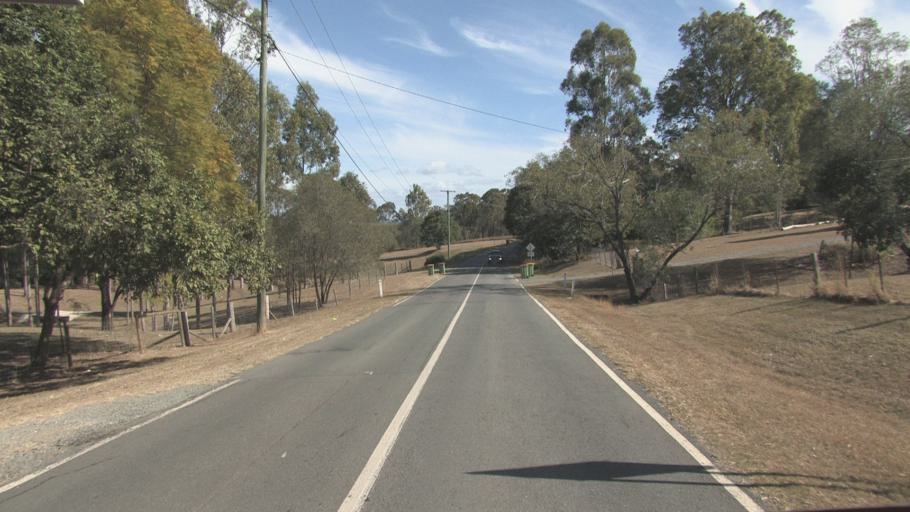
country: AU
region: Queensland
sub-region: Logan
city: Cedar Vale
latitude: -27.8808
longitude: 152.9901
